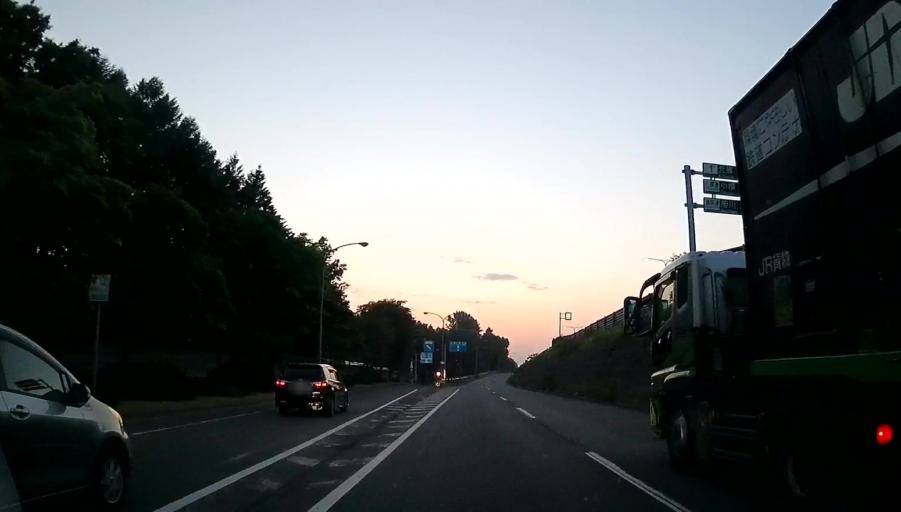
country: JP
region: Hokkaido
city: Sapporo
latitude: 43.0245
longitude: 141.4527
